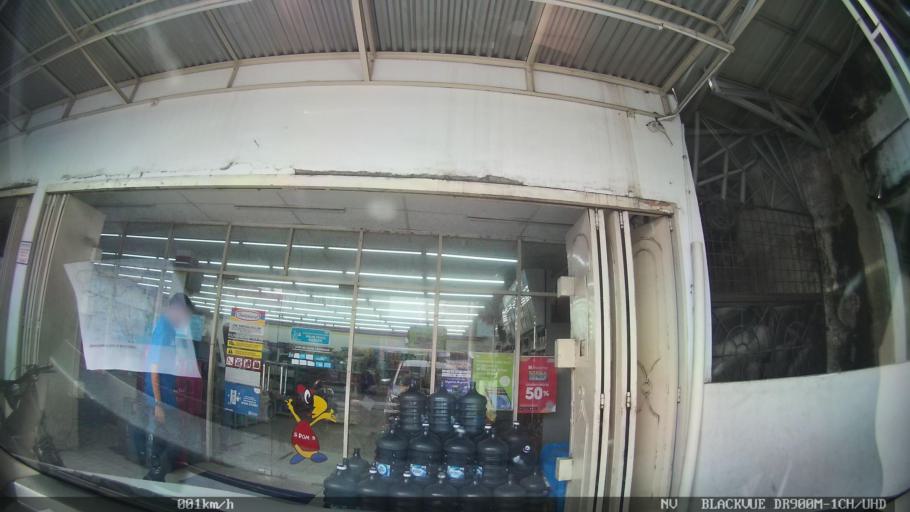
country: ID
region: North Sumatra
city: Medan
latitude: 3.6072
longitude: 98.7585
